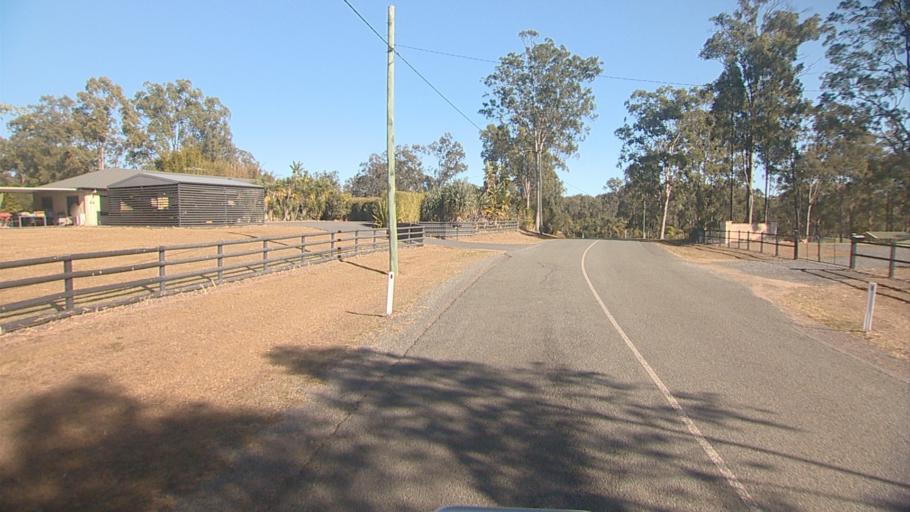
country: AU
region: Queensland
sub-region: Logan
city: Cedar Vale
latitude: -27.8824
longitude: 153.0032
